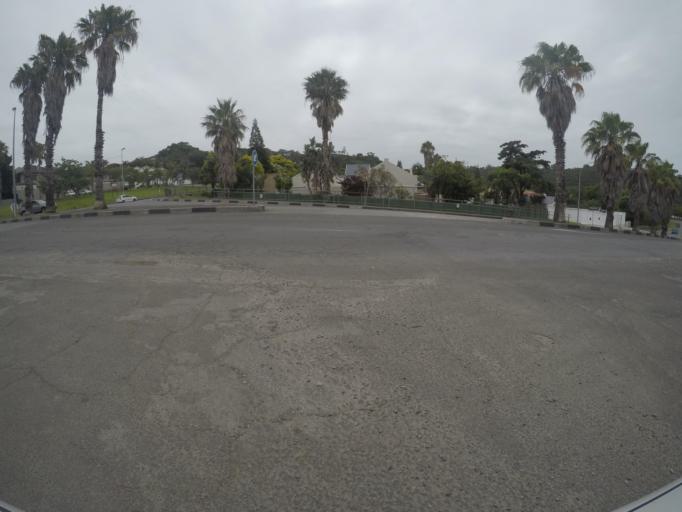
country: ZA
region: Eastern Cape
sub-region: Buffalo City Metropolitan Municipality
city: East London
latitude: -32.9734
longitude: 27.9281
